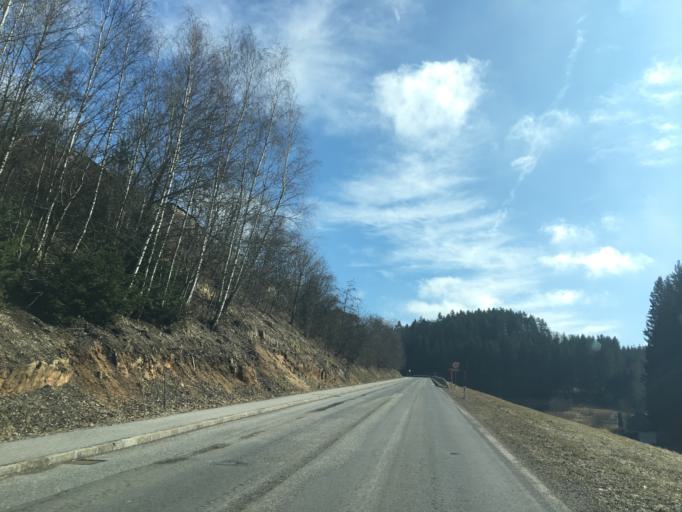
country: AT
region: Upper Austria
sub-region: Politischer Bezirk Perg
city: Sankt Georgen am Walde
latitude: 48.4036
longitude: 14.8419
